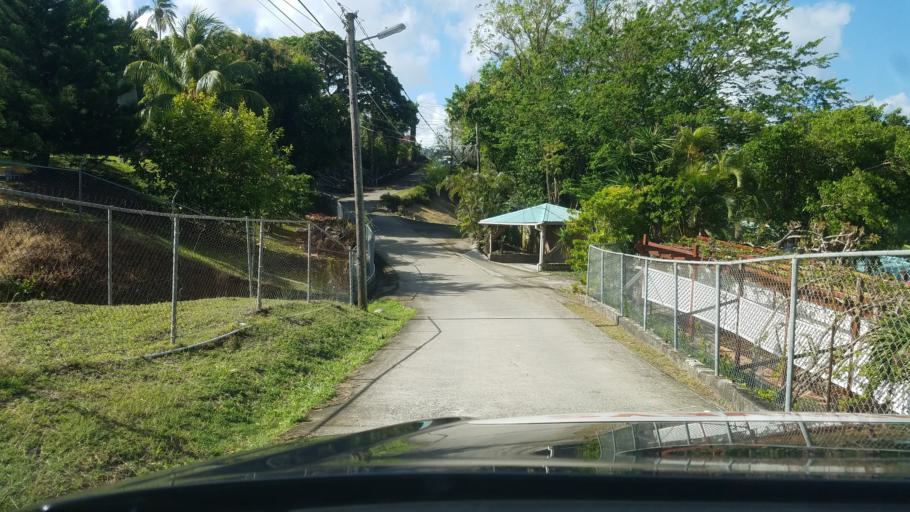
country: LC
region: Castries Quarter
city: Castries
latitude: 14.0233
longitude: -61.0042
